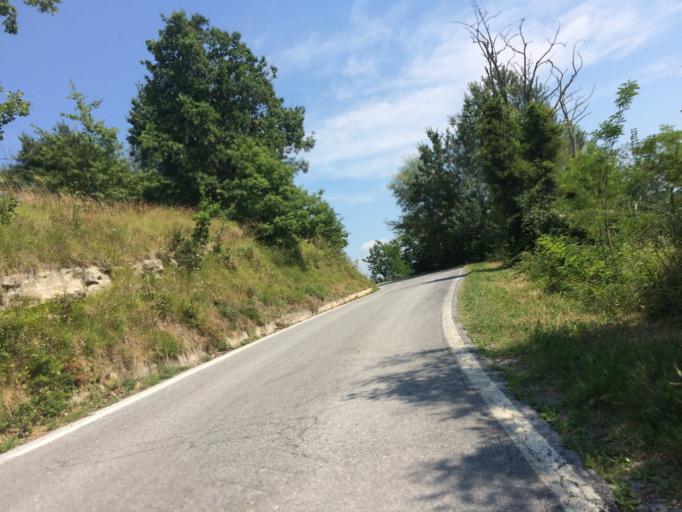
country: IT
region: Piedmont
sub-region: Provincia di Cuneo
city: Cissone
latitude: 44.5595
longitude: 8.0439
